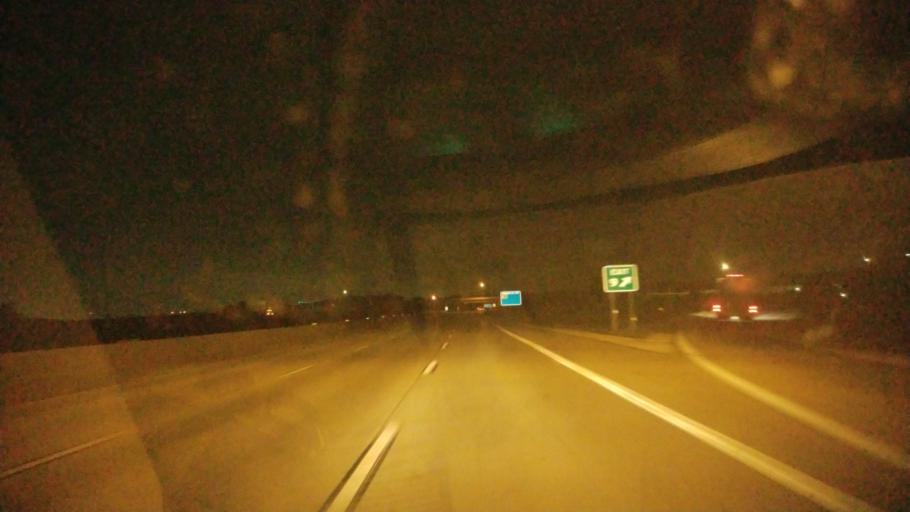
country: US
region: Missouri
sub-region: Saint Charles County
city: Saint Charles
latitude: 38.7920
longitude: -90.4473
